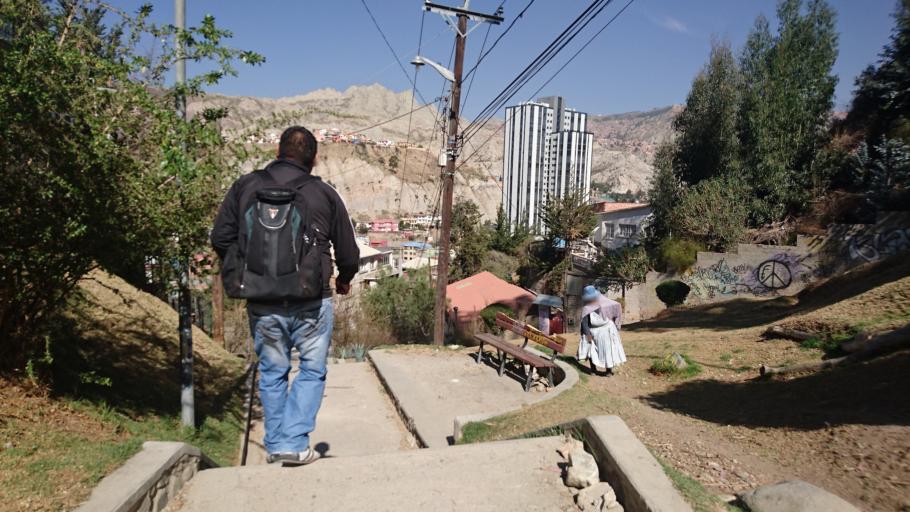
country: BO
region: La Paz
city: La Paz
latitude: -16.5294
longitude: -68.0981
